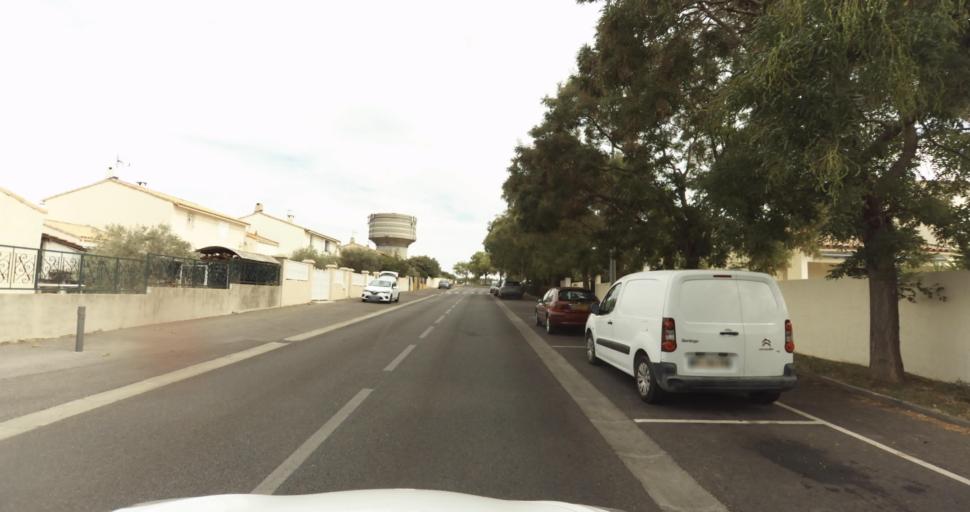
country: FR
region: Provence-Alpes-Cote d'Azur
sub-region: Departement des Bouches-du-Rhone
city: Miramas
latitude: 43.5738
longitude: 5.0031
